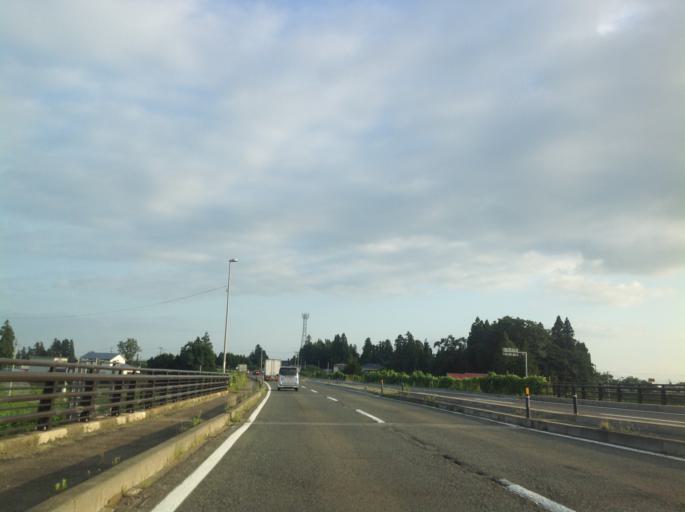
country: JP
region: Iwate
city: Hanamaki
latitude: 39.4768
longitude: 141.1390
